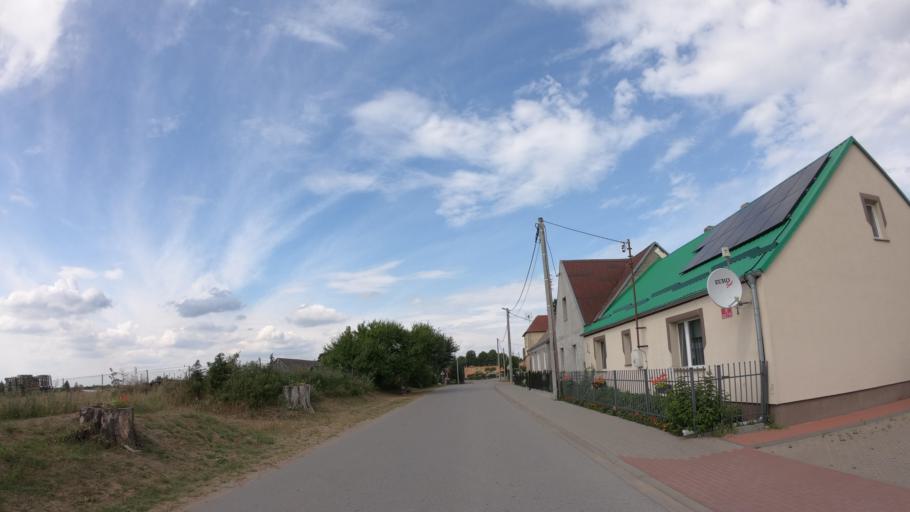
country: PL
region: West Pomeranian Voivodeship
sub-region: Powiat walecki
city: Tuczno
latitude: 53.2445
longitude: 16.1378
